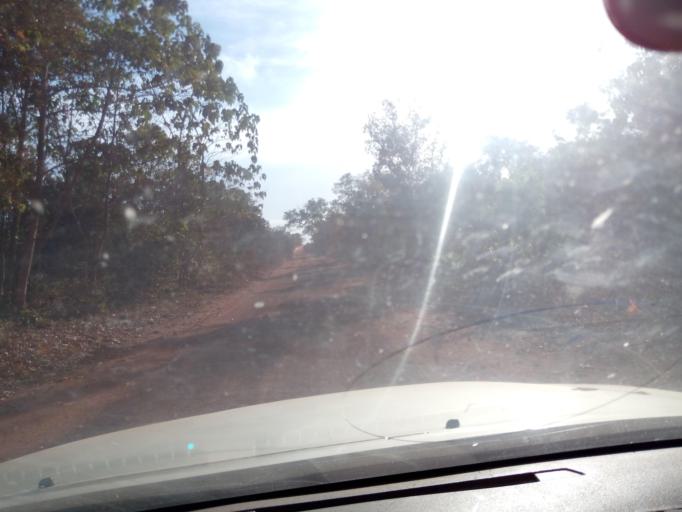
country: ML
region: Sikasso
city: Sikasso
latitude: 11.4279
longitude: -5.5586
